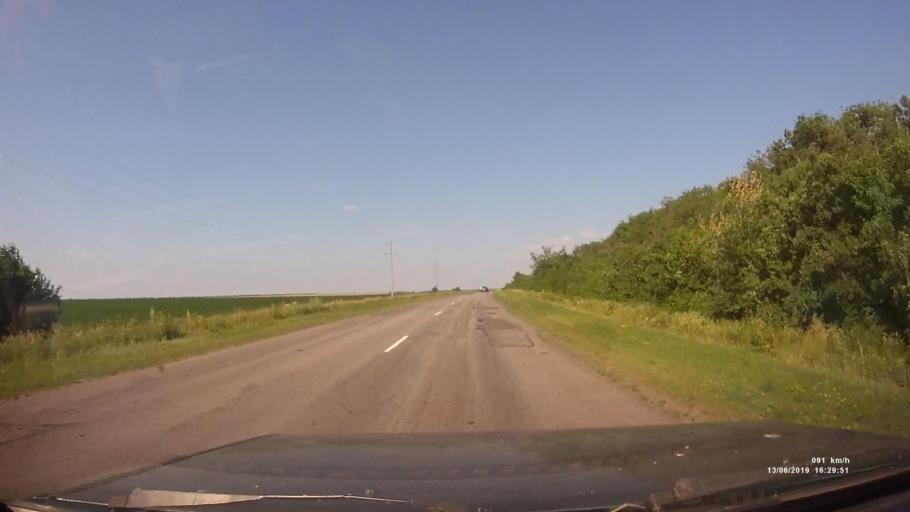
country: RU
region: Rostov
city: Kazanskaya
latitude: 49.8336
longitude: 41.2238
